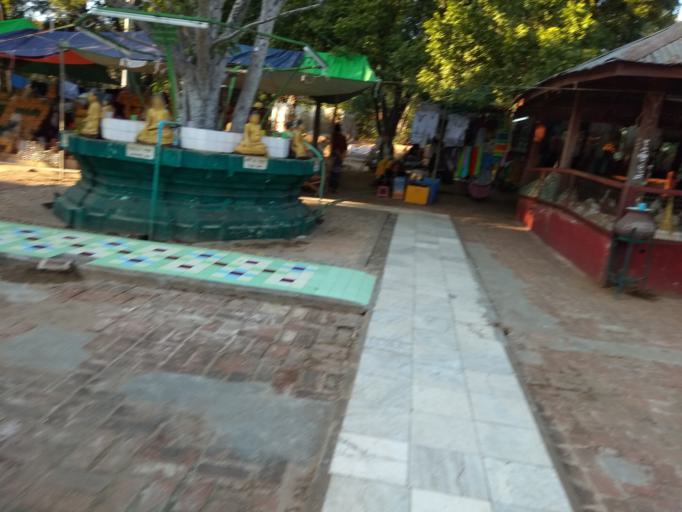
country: MM
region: Magway
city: Chauk
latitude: 21.1575
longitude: 94.8615
